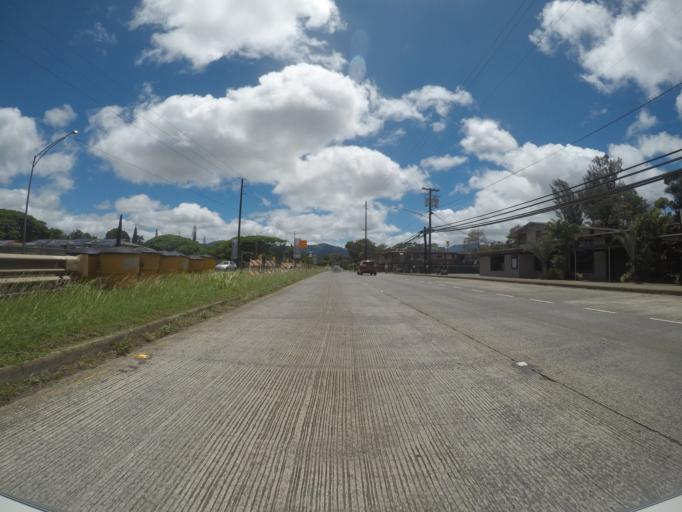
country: US
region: Hawaii
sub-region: Honolulu County
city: Wahiawa
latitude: 21.4901
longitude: -158.0330
